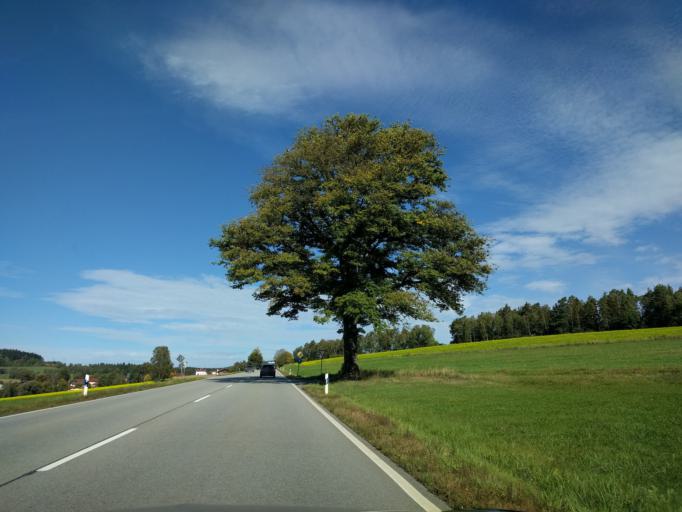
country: DE
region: Bavaria
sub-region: Lower Bavaria
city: Patersdorf
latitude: 49.0188
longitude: 12.9773
